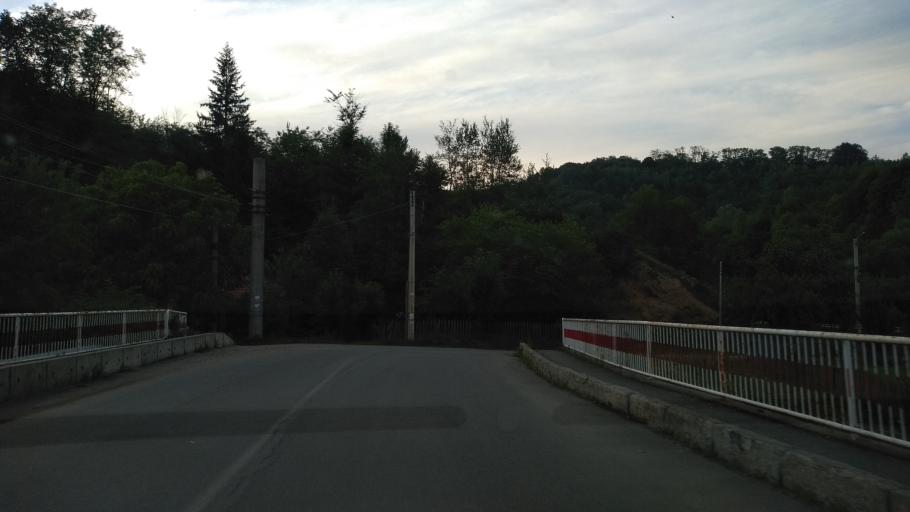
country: RO
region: Hunedoara
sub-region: Comuna Aninoasa
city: Iscroni
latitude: 45.3851
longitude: 23.3272
